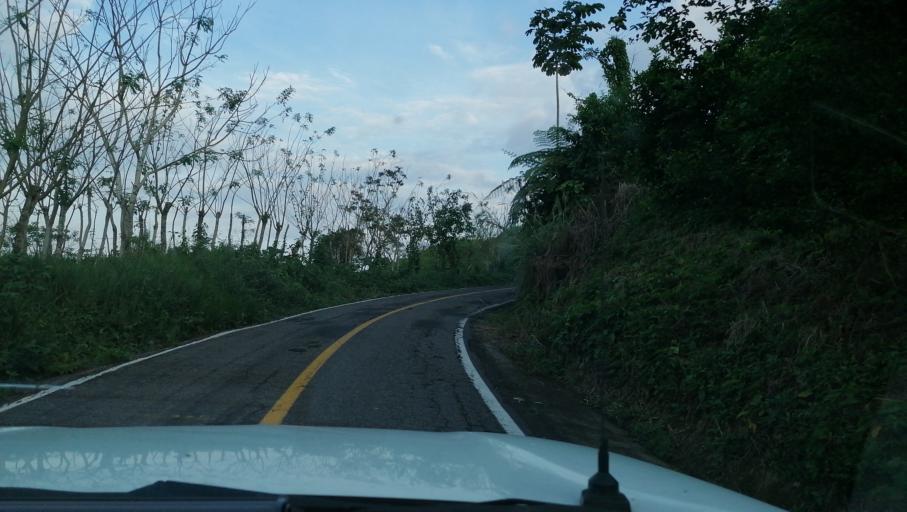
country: MX
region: Chiapas
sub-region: Juarez
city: El Triunfo 1ra. Seccion (Cardona)
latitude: 17.5065
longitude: -93.2278
